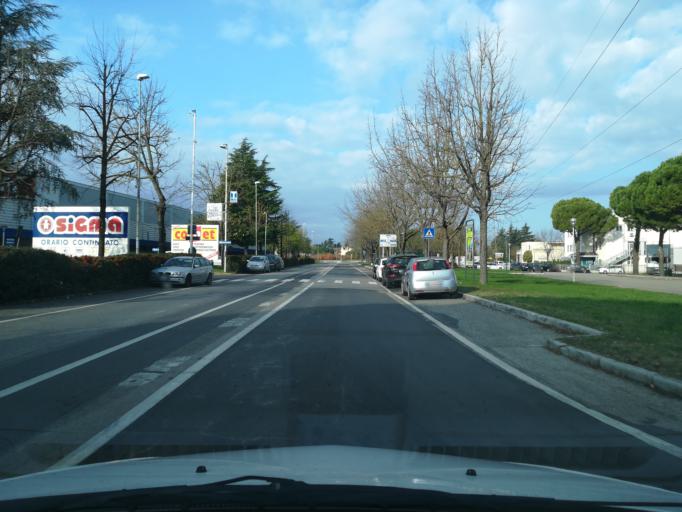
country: IT
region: Emilia-Romagna
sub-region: Provincia di Bologna
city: Imola
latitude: 44.3674
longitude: 11.7064
